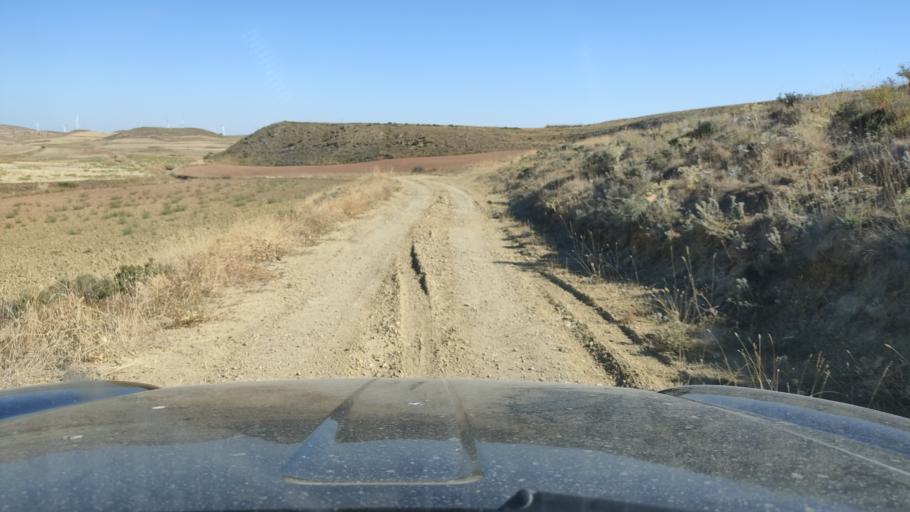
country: ES
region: Aragon
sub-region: Provincia de Teruel
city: Monforte de Moyuela
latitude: 41.0360
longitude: -0.9980
